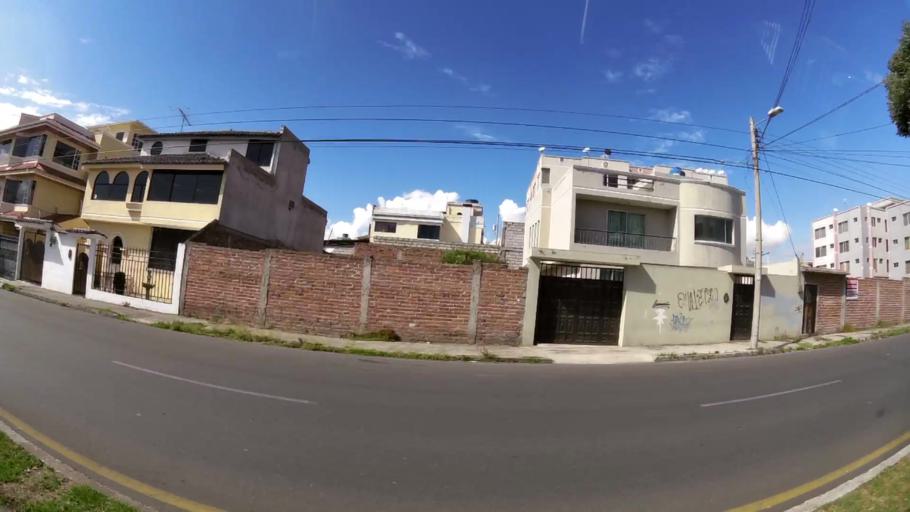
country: EC
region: Chimborazo
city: Riobamba
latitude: -1.6640
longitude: -78.6658
